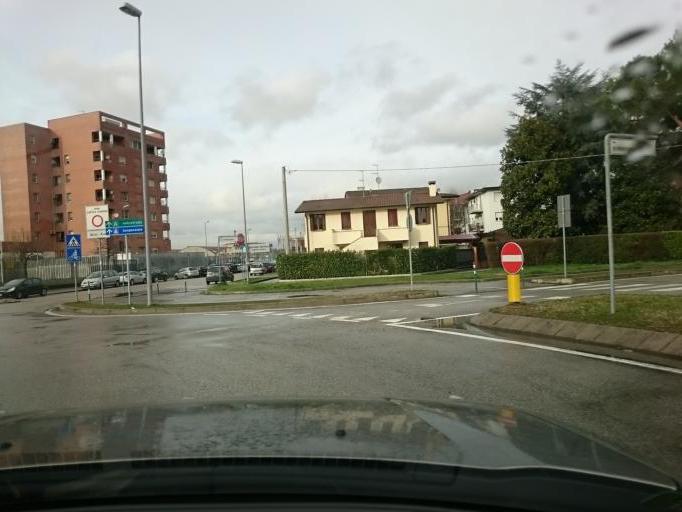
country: IT
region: Veneto
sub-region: Provincia di Padova
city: Padova
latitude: 45.4132
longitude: 11.8969
